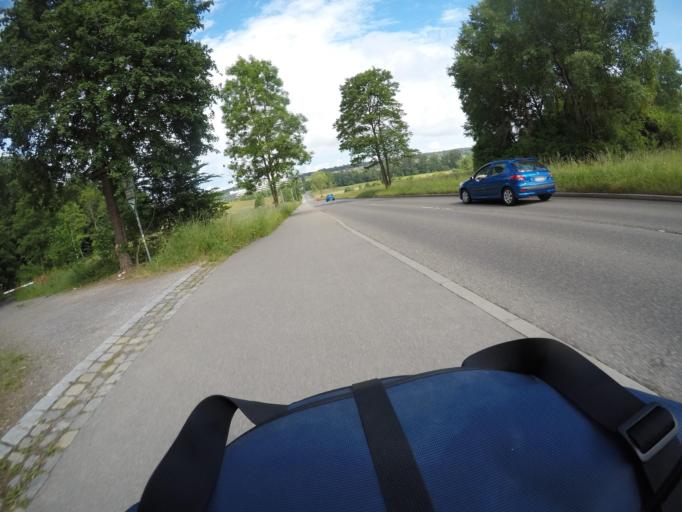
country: DE
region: Baden-Wuerttemberg
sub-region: Regierungsbezirk Stuttgart
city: Gerlingen
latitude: 48.7416
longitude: 9.0881
